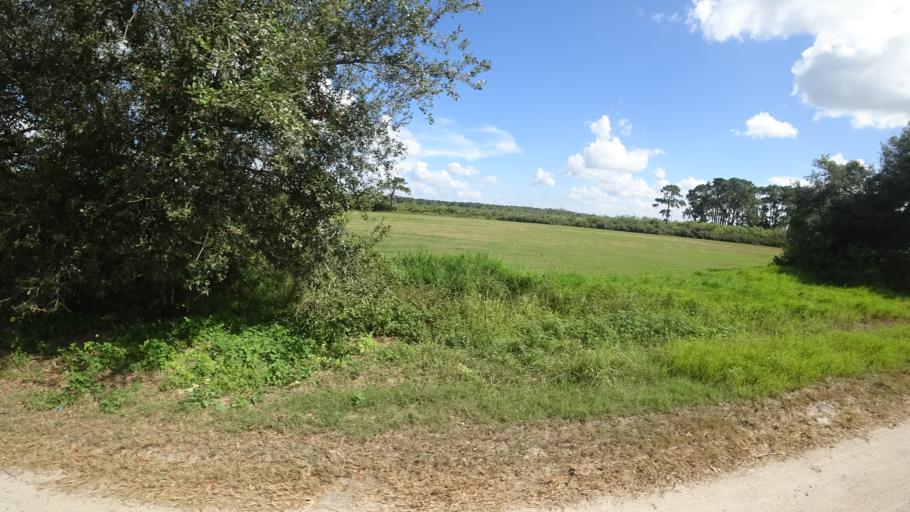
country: US
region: Florida
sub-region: Sarasota County
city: Warm Mineral Springs
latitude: 27.3180
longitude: -82.1304
